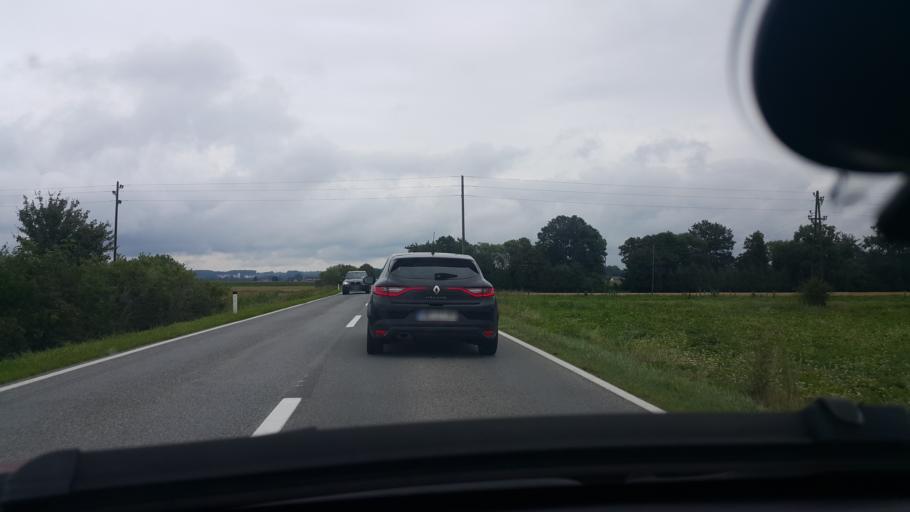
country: SI
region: Zavrc
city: Zavrc
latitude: 46.4145
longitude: 16.0539
